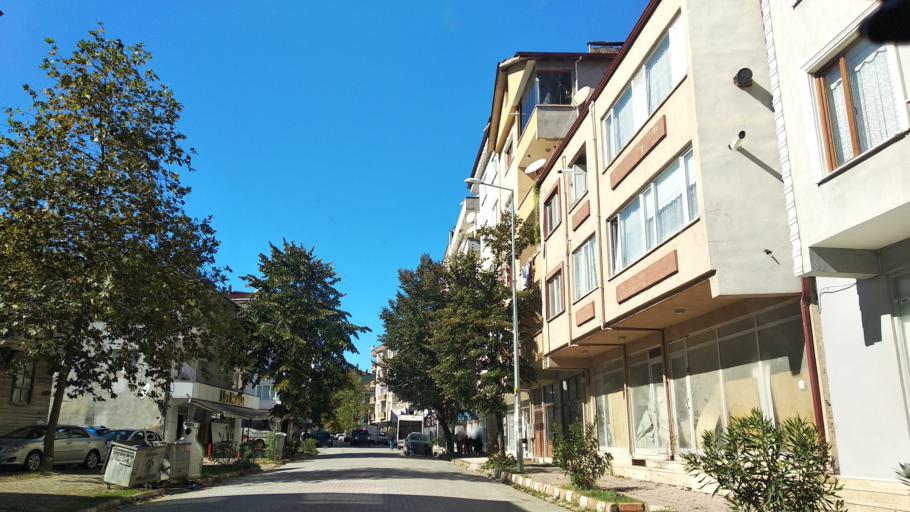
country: TR
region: Sakarya
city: Karasu
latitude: 41.0924
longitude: 30.6950
